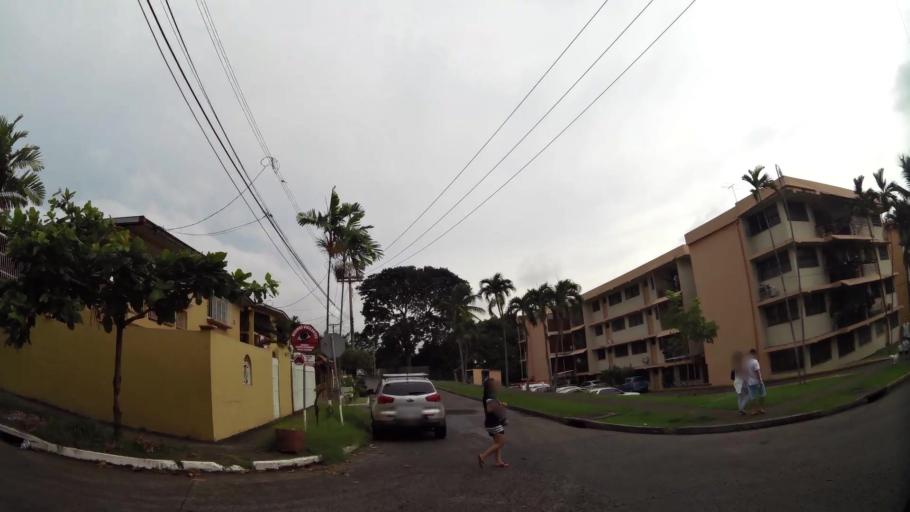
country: PA
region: Panama
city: Panama
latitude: 9.0078
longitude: -79.5330
